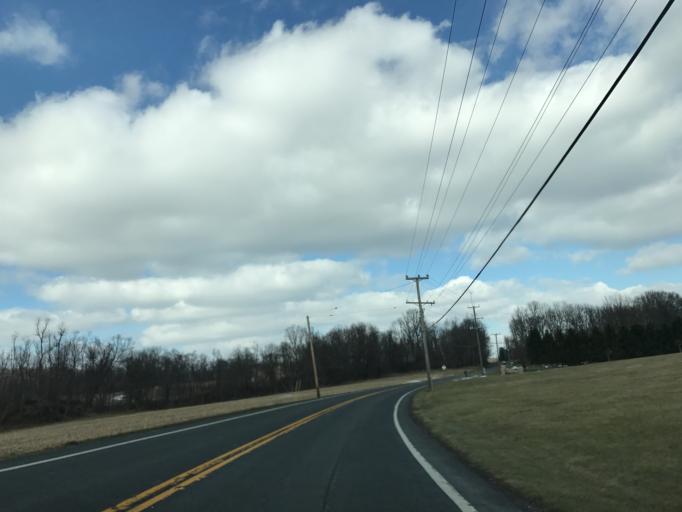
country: US
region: Maryland
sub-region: Carroll County
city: Manchester
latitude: 39.6782
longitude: -76.9282
